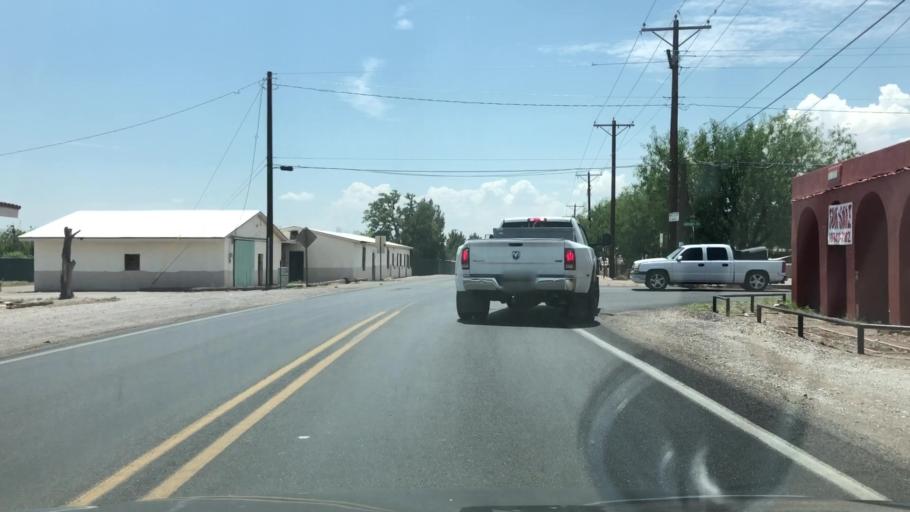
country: US
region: New Mexico
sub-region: Dona Ana County
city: La Union
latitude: 31.9553
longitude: -106.6451
